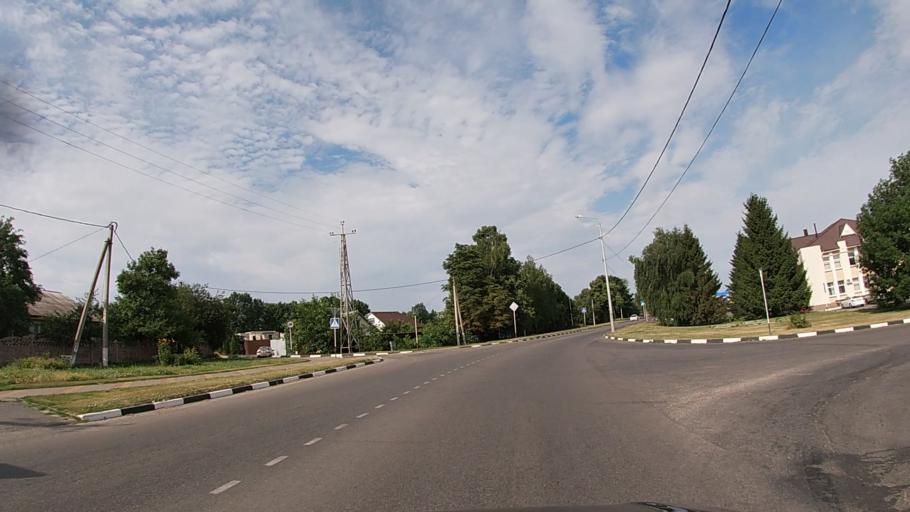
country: RU
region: Belgorod
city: Krasnaya Yaruga
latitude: 50.7989
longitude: 35.6508
